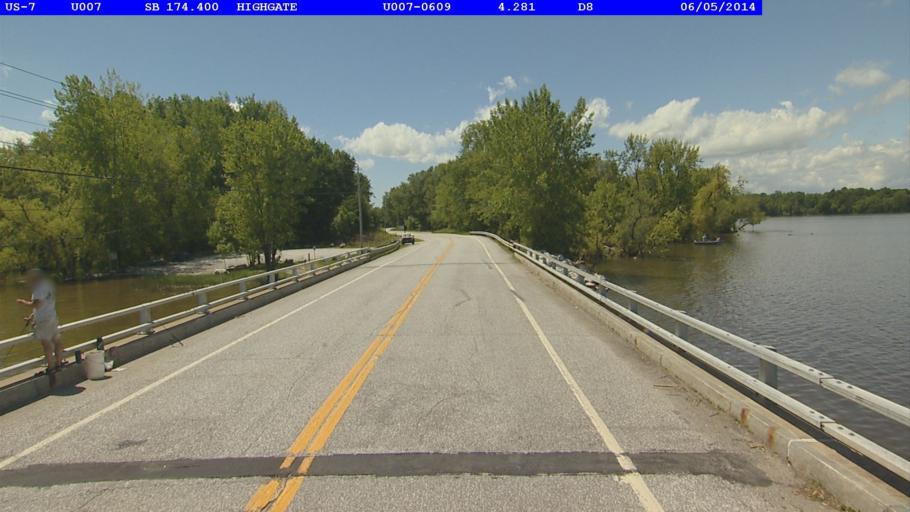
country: US
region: Vermont
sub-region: Franklin County
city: Swanton
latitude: 44.9891
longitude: -73.0882
